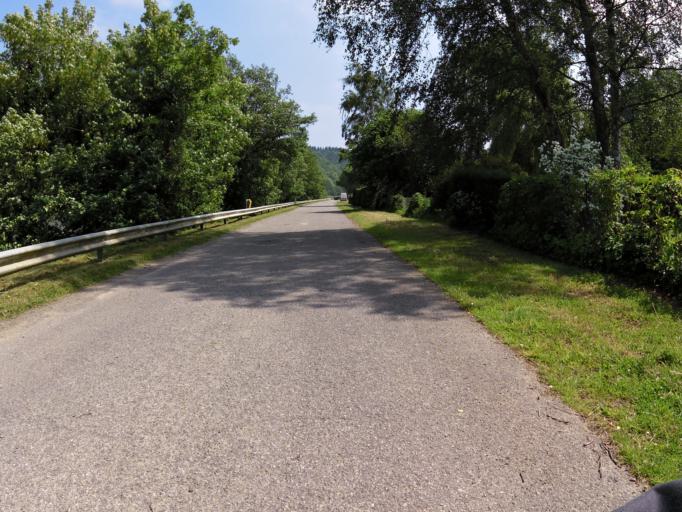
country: BE
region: Wallonia
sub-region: Province de Namur
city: Hastiere-Lavaux
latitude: 50.2136
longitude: 4.8422
